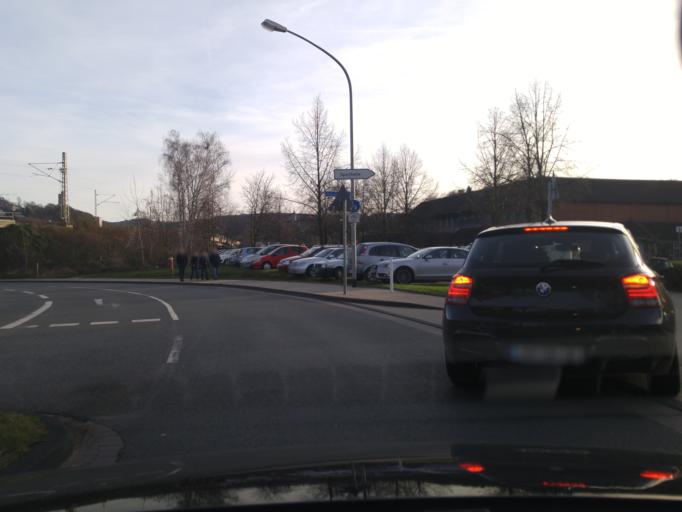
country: DE
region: North Rhine-Westphalia
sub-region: Regierungsbezirk Dusseldorf
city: Velbert
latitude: 51.3931
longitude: 7.0784
